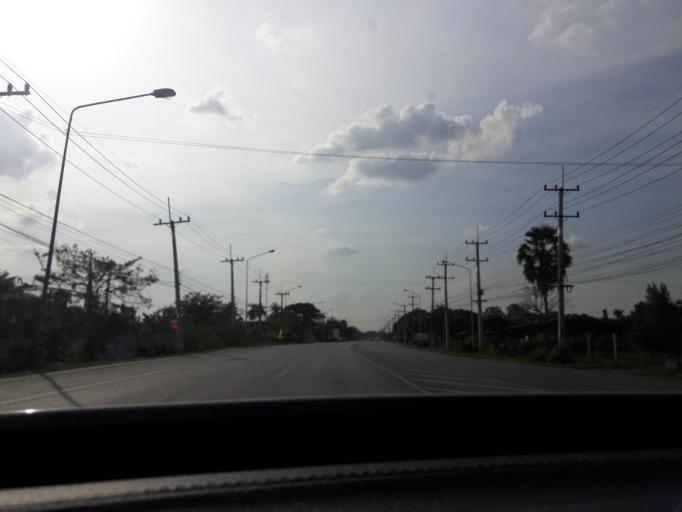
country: TH
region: Sing Buri
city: Sing Buri
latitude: 14.8544
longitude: 100.3862
